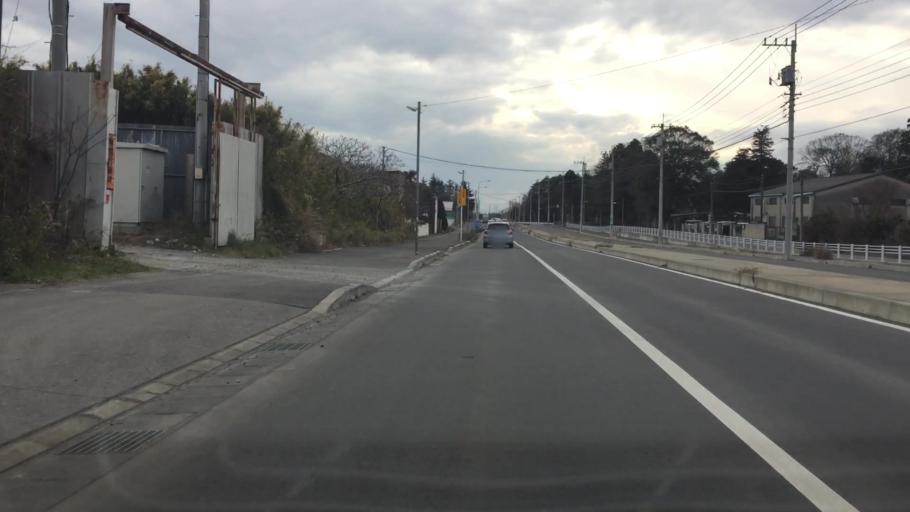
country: JP
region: Chiba
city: Shiroi
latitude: 35.8004
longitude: 140.0965
